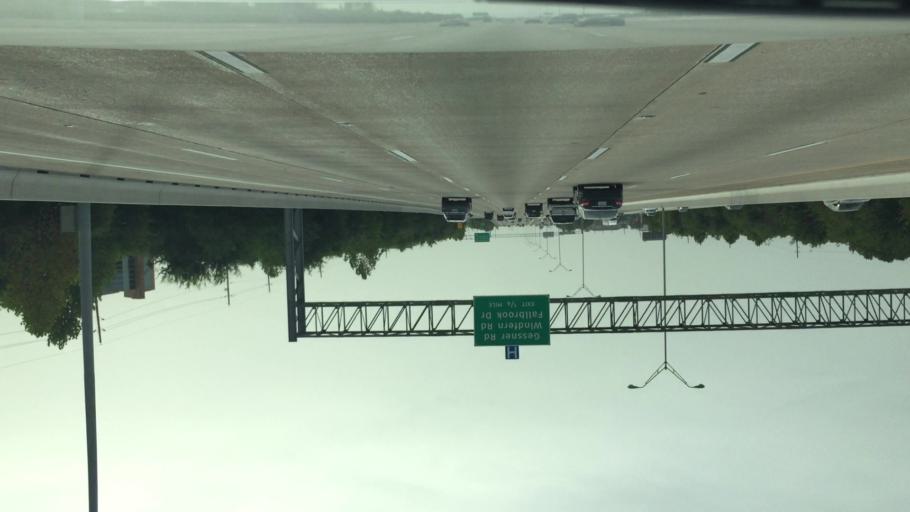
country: US
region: Texas
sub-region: Harris County
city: Hudson
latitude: 29.9332
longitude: -95.5362
